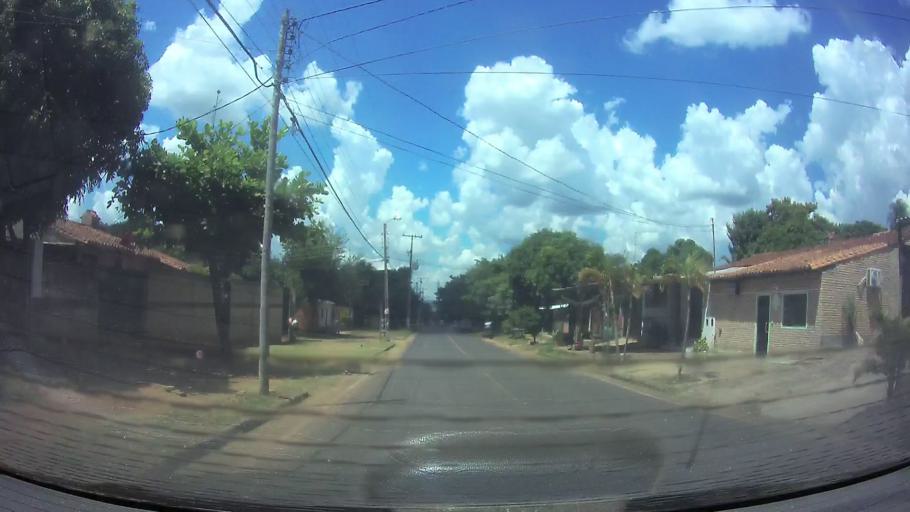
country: PY
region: Central
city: Limpio
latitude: -25.1678
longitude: -57.4394
